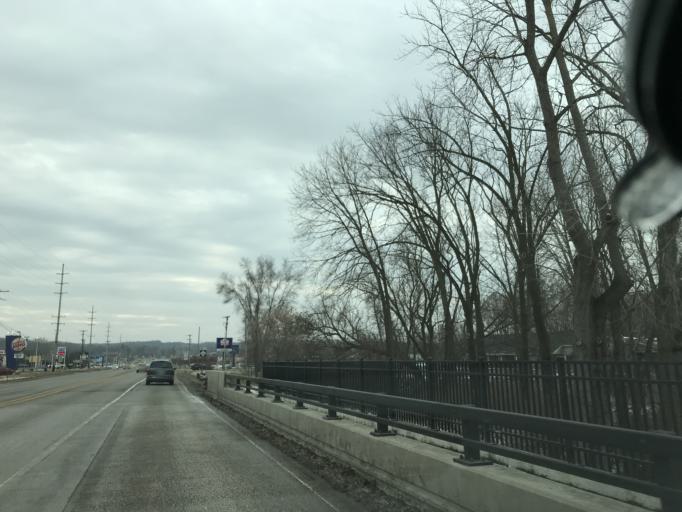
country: US
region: Michigan
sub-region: Kent County
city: Northview
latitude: 43.0633
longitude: -85.5800
